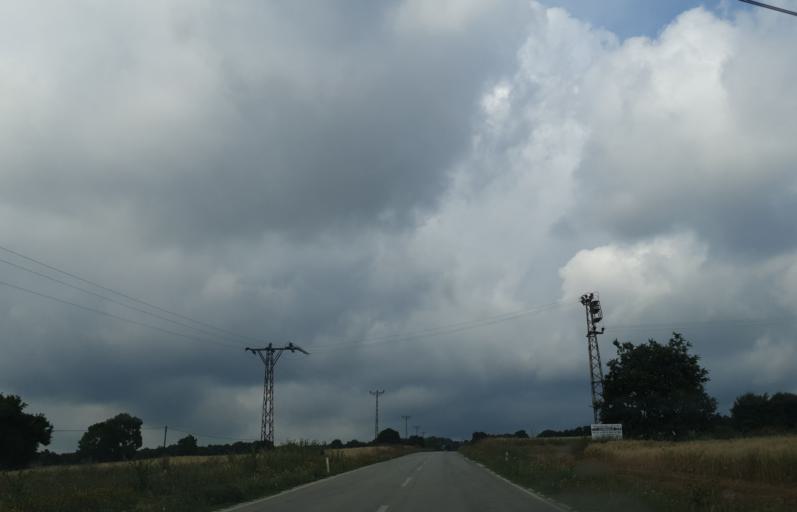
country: TR
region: Tekirdag
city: Saray
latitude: 41.4836
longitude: 27.9636
